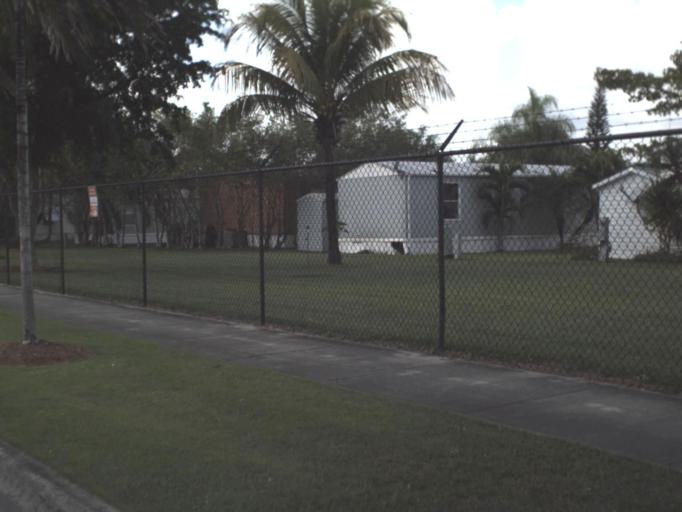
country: US
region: Florida
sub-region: Miami-Dade County
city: Leisure City
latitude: 25.4995
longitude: -80.4358
